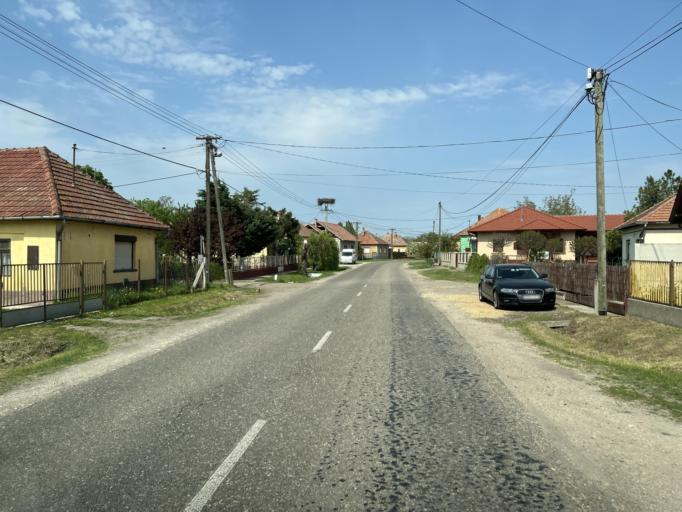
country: HU
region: Pest
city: Tortel
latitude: 47.1189
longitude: 19.9471
